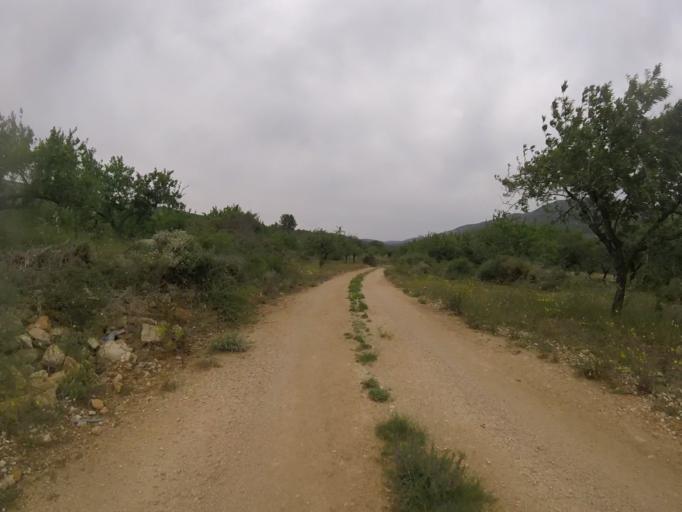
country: ES
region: Valencia
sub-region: Provincia de Castello
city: Alcala de Xivert
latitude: 40.2867
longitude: 0.2575
